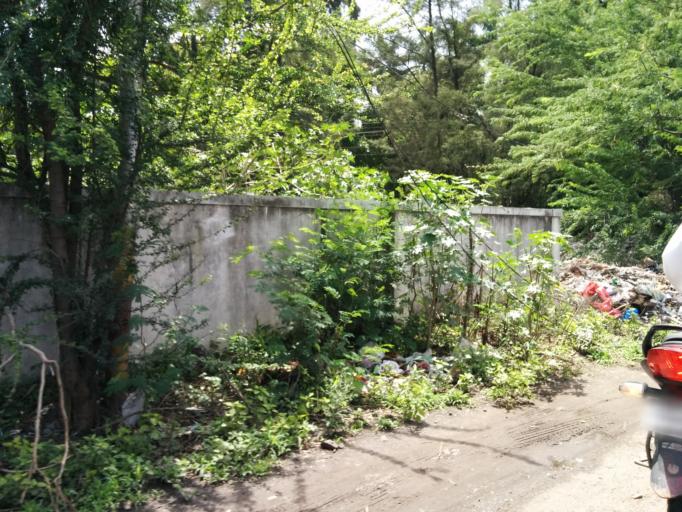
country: IN
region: Maharashtra
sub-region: Pune Division
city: Pune
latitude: 18.5328
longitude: 73.9166
